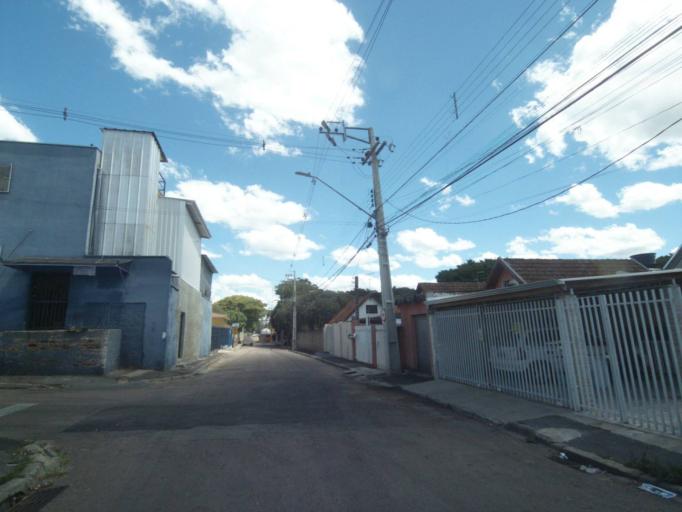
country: BR
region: Parana
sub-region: Curitiba
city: Curitiba
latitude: -25.5027
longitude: -49.3236
